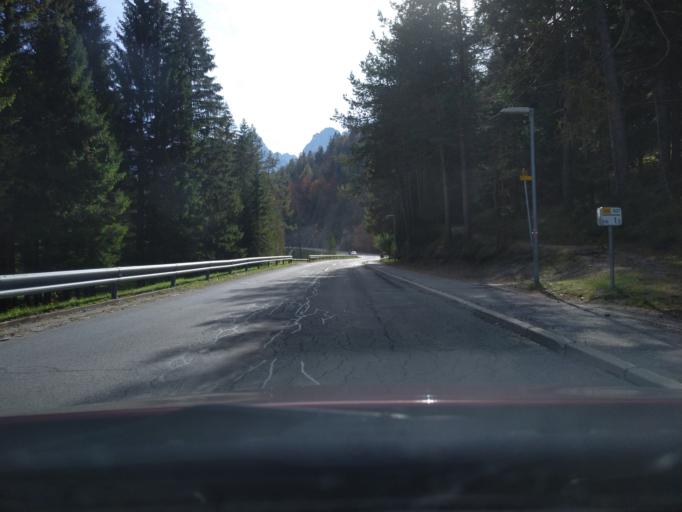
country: SI
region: Kranjska Gora
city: Kranjska Gora
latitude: 46.4781
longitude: 13.7802
